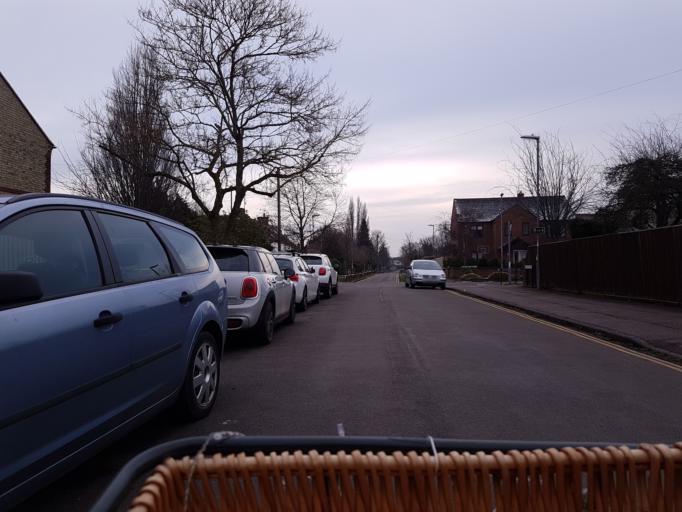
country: GB
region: England
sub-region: Cambridgeshire
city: Cambridge
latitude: 52.1855
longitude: 0.1447
